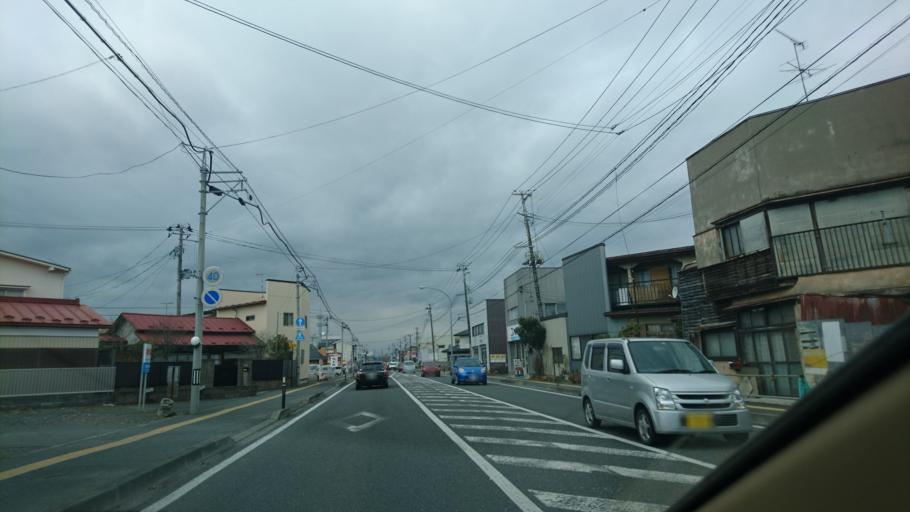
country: JP
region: Miyagi
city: Furukawa
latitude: 38.5787
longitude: 140.9606
